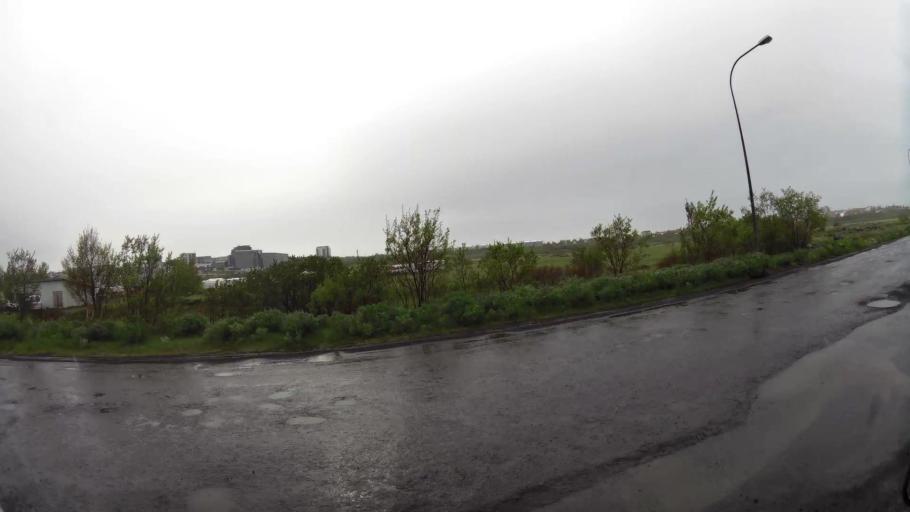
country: IS
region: Capital Region
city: Reykjavik
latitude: 64.0991
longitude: -21.7936
